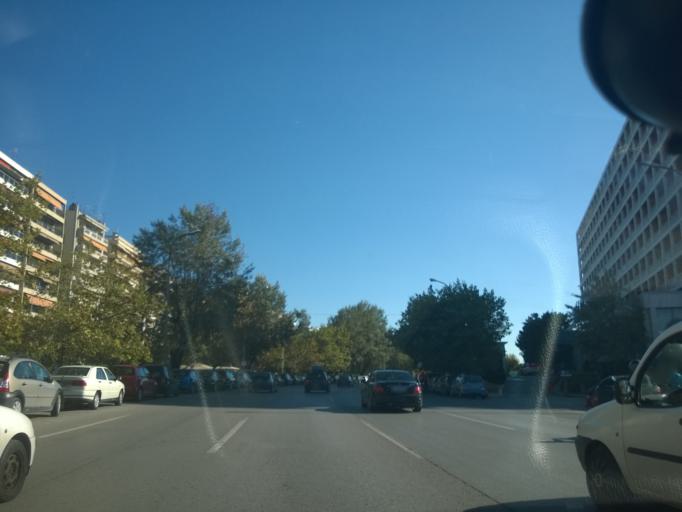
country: GR
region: Central Macedonia
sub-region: Nomos Thessalonikis
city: Agios Pavlos
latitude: 40.6189
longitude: 22.9531
